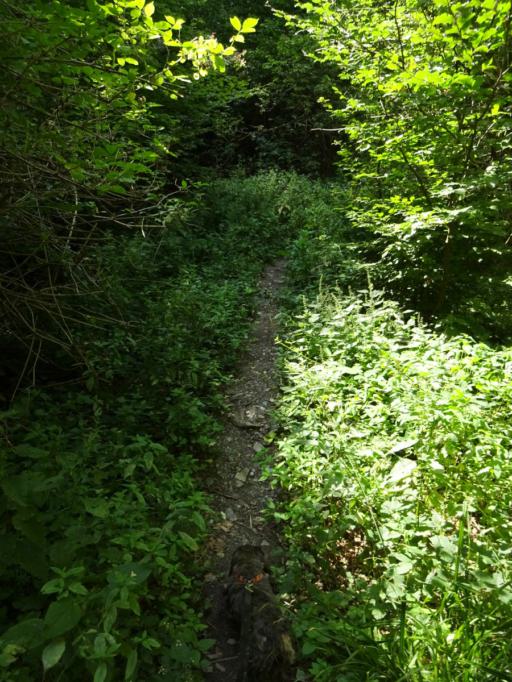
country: AT
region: Burgenland
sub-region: Politischer Bezirk Oberwart
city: Rechnitz
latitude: 47.3476
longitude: 16.4629
